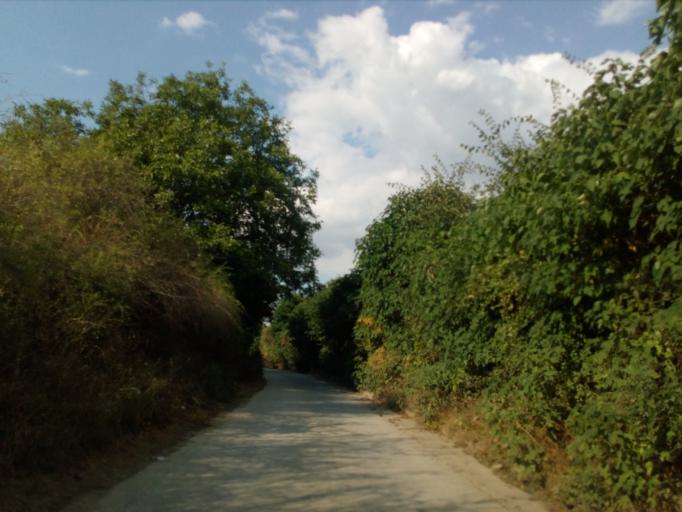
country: MK
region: Veles
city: Veles
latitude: 41.7454
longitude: 21.7913
